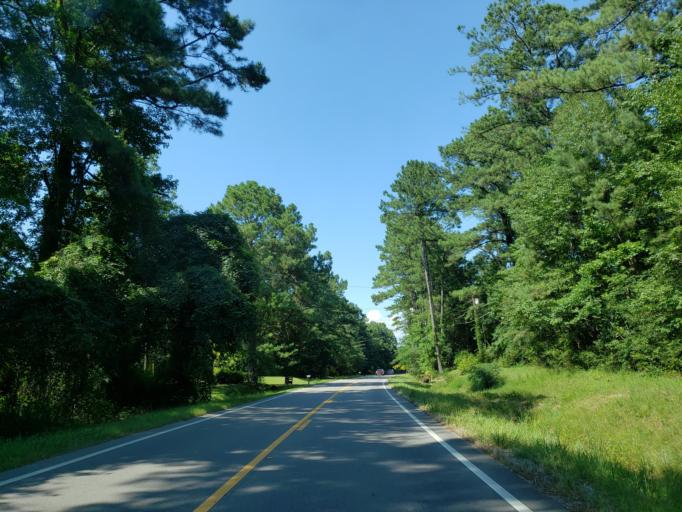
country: US
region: Mississippi
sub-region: Lamar County
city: Sumrall
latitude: 31.4261
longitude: -89.5453
